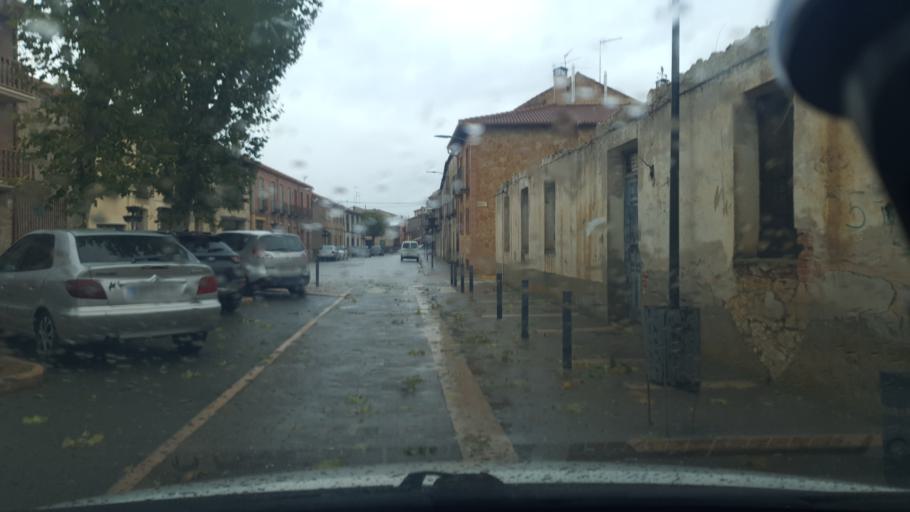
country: ES
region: Castille and Leon
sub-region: Provincia de Segovia
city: Carbonero el Mayor
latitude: 41.1200
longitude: -4.2647
